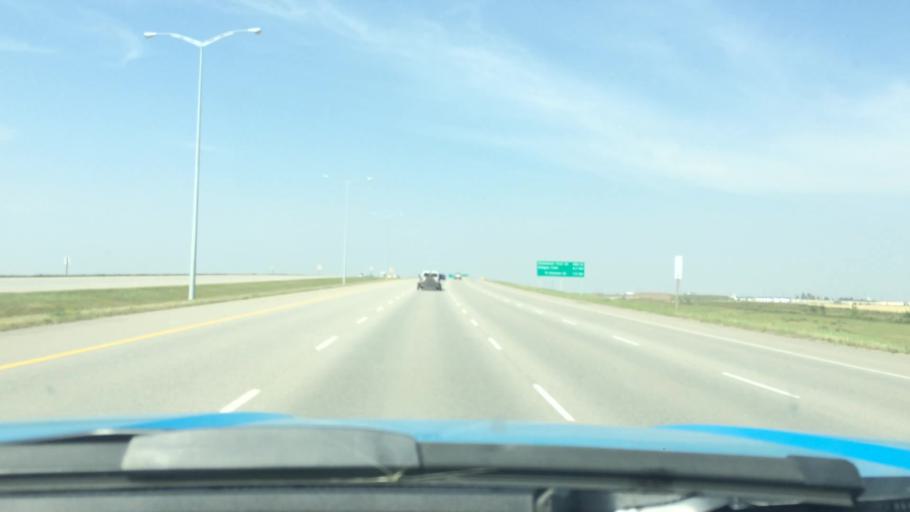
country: CA
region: Alberta
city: Chestermere
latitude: 50.9662
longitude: -113.9206
